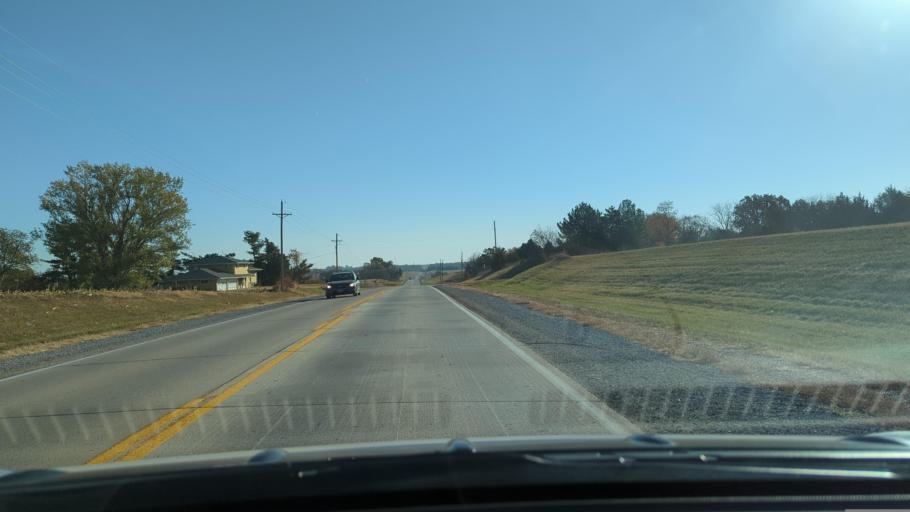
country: US
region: Nebraska
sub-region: Sarpy County
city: Papillion
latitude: 41.0926
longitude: -96.0204
